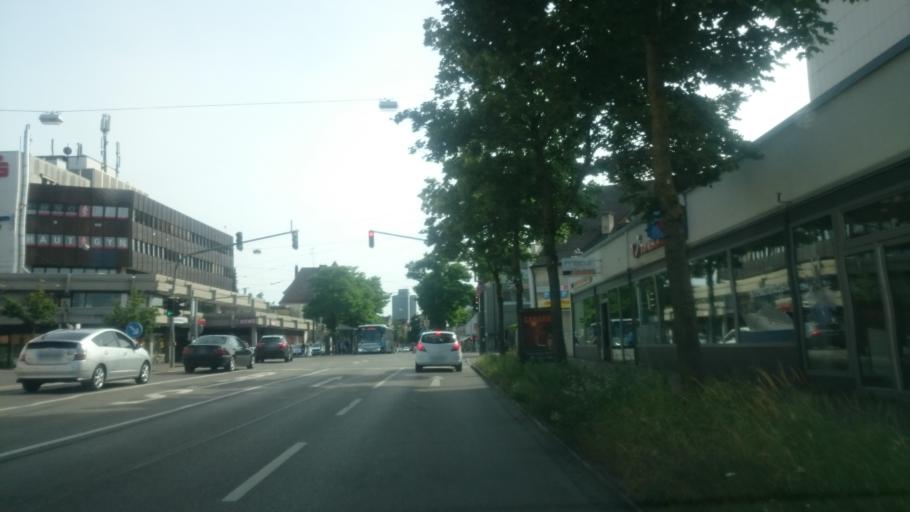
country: DE
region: Bavaria
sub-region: Swabia
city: Augsburg
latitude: 48.3817
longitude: 10.9164
